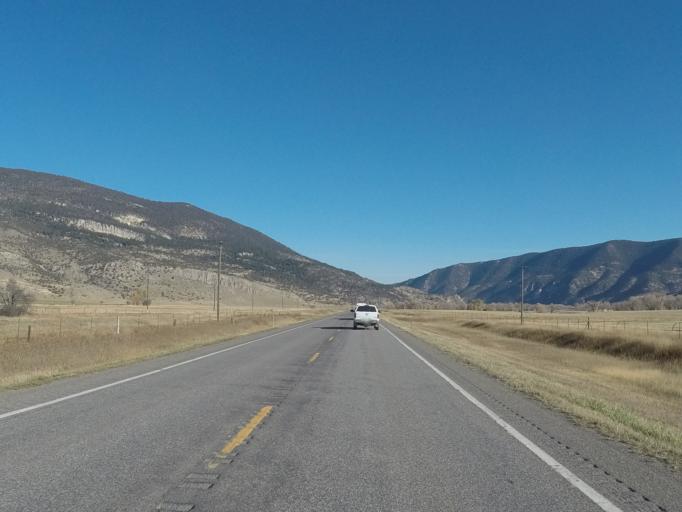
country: US
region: Montana
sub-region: Park County
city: Livingston
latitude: 45.5578
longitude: -110.5944
